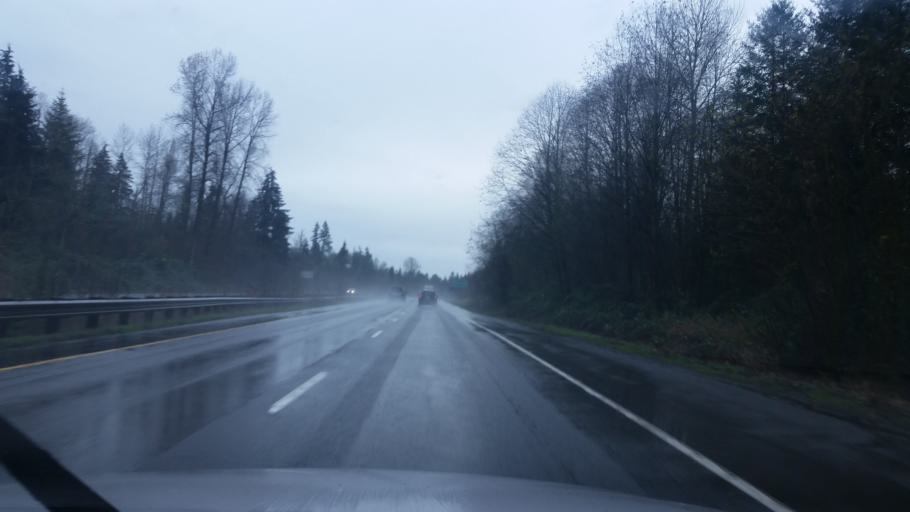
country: US
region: Washington
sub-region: King County
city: Hobart
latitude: 47.4286
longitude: -121.9892
